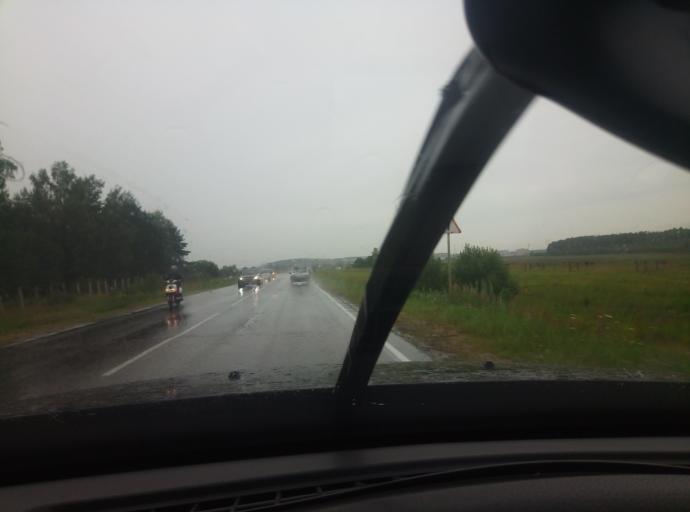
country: RU
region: Kaluga
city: Kremenki
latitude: 54.8775
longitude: 37.1431
